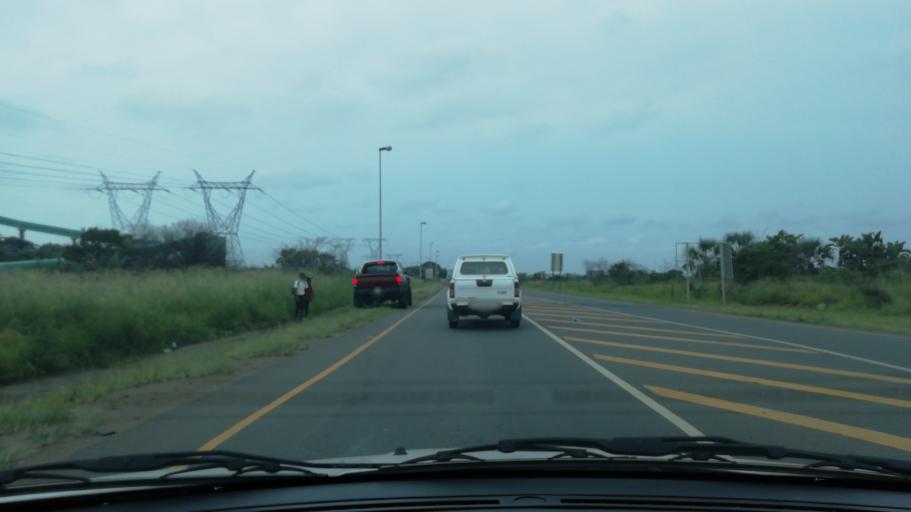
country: ZA
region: KwaZulu-Natal
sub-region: uThungulu District Municipality
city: Richards Bay
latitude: -28.7673
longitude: 32.0361
